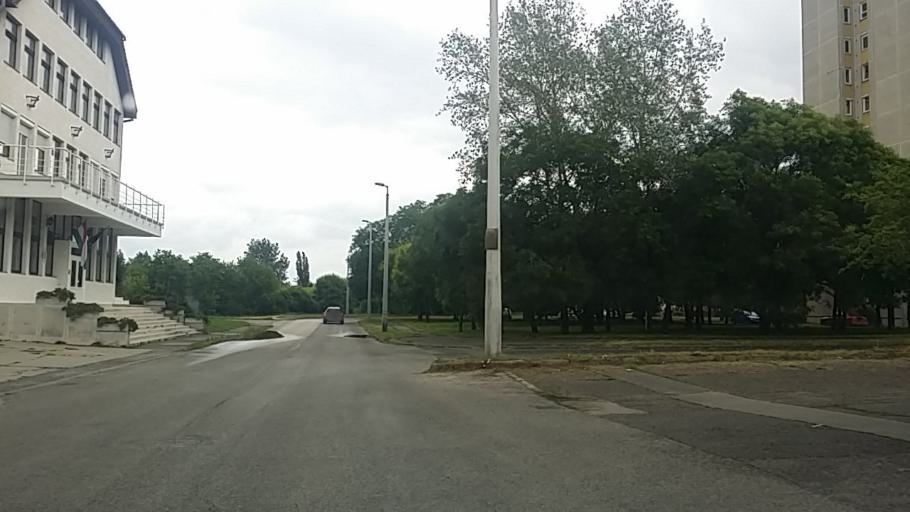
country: HU
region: Budapest
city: Budapest XXI. keruelet
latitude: 47.4262
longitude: 19.0866
